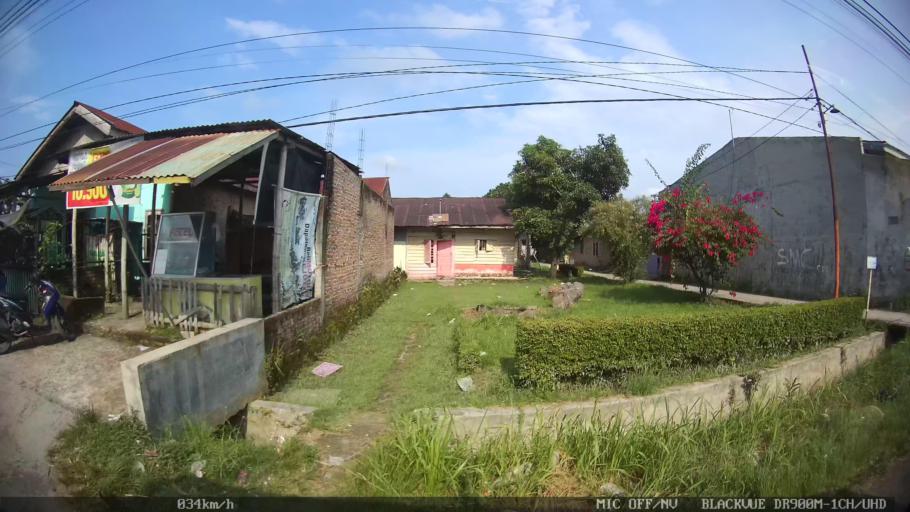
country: ID
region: North Sumatra
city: Medan
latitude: 3.5784
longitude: 98.7567
